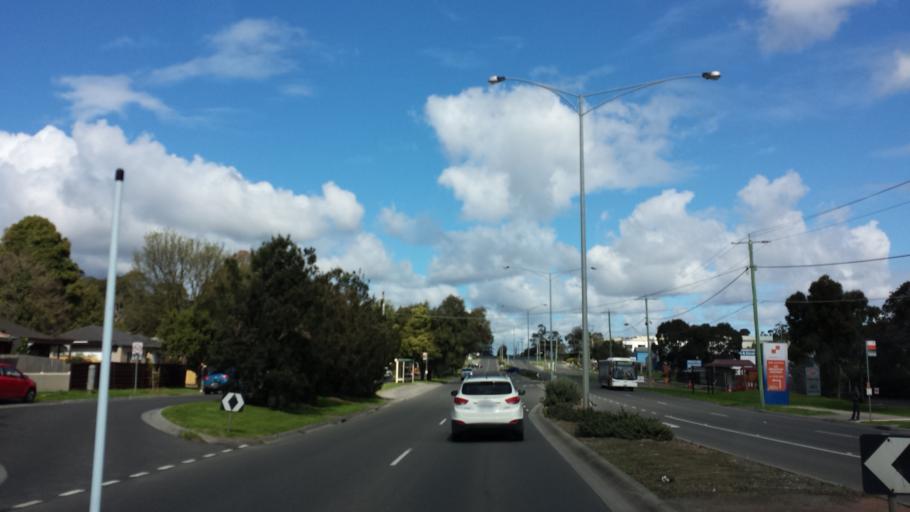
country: AU
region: Victoria
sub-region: Maroondah
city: Bayswater North
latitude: -37.8401
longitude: 145.2870
